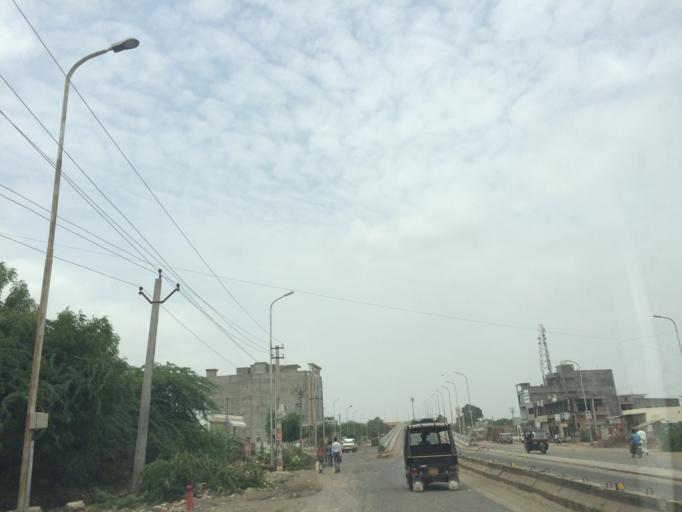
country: IN
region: Rajasthan
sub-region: Barmer
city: Barmer
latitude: 25.7581
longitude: 71.4153
